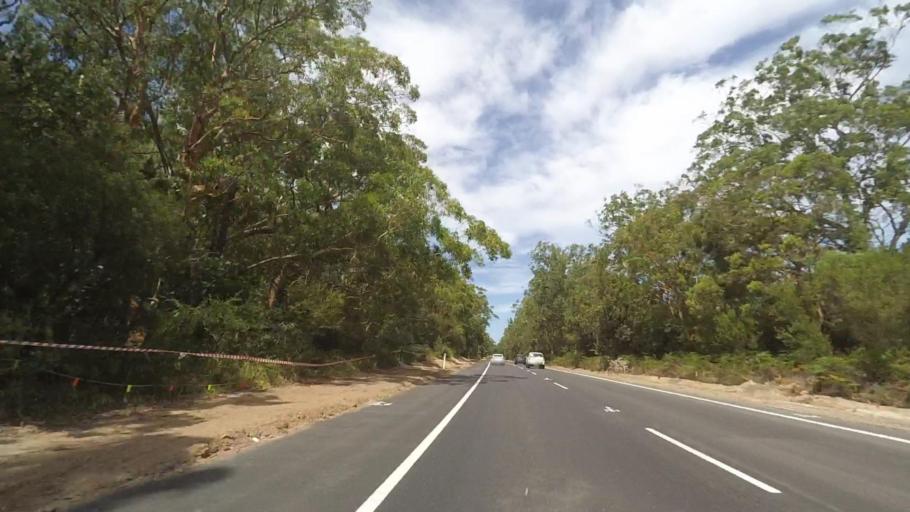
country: AU
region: New South Wales
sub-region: Port Stephens Shire
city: Anna Bay
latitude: -32.7796
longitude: 151.9957
